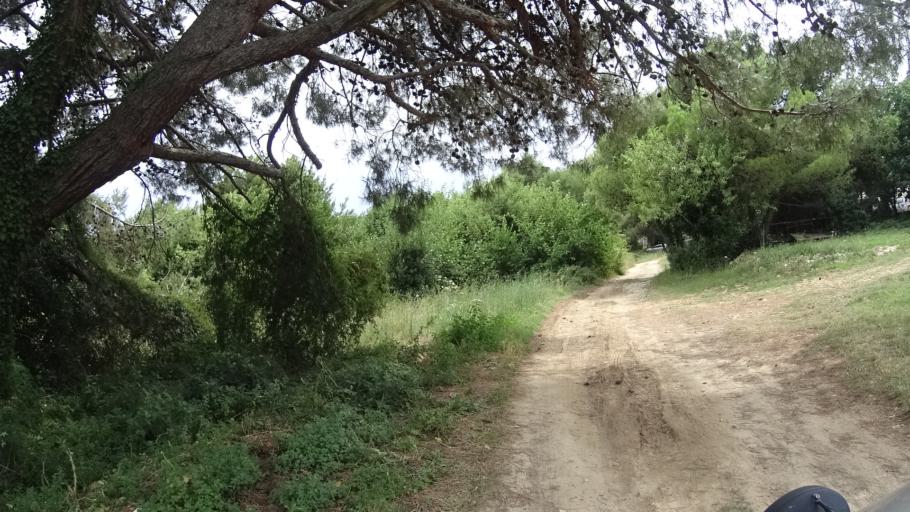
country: HR
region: Istarska
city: Medulin
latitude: 44.7998
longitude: 13.9147
